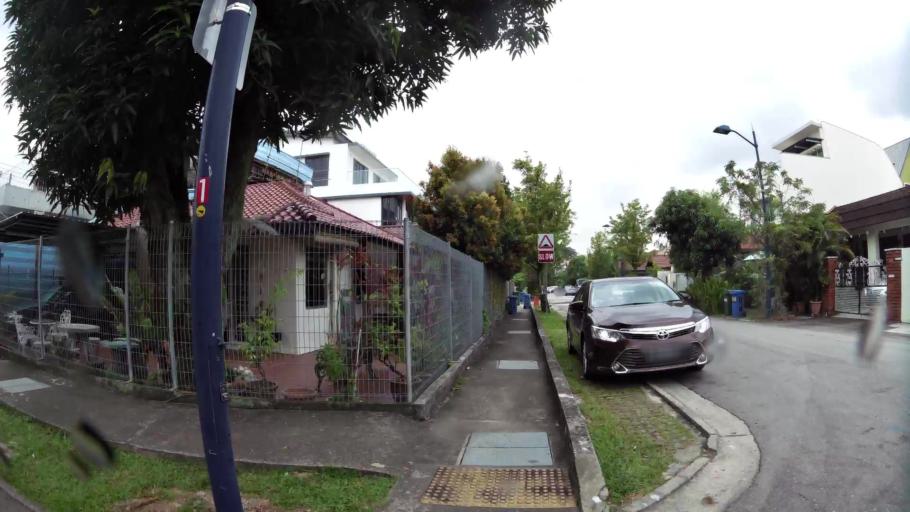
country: SG
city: Singapore
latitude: 1.3677
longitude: 103.8652
